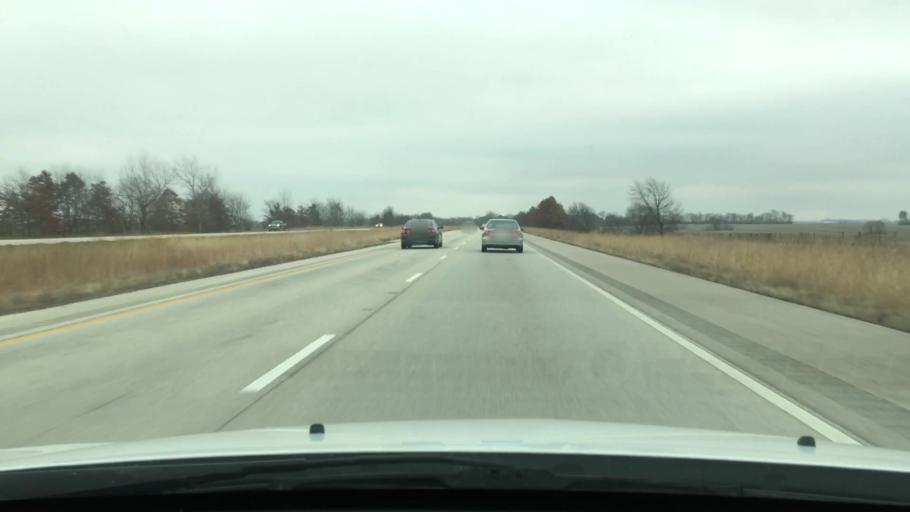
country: US
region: Illinois
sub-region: Sangamon County
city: New Berlin
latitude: 39.7410
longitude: -89.8391
